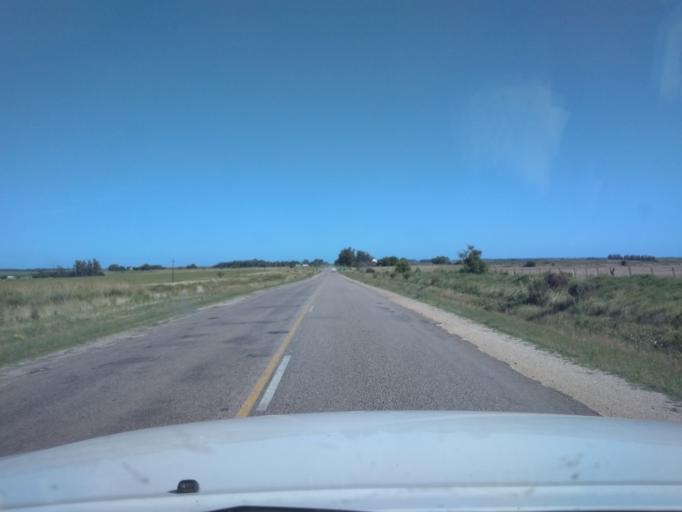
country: UY
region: Canelones
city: San Ramon
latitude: -34.2078
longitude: -55.9308
